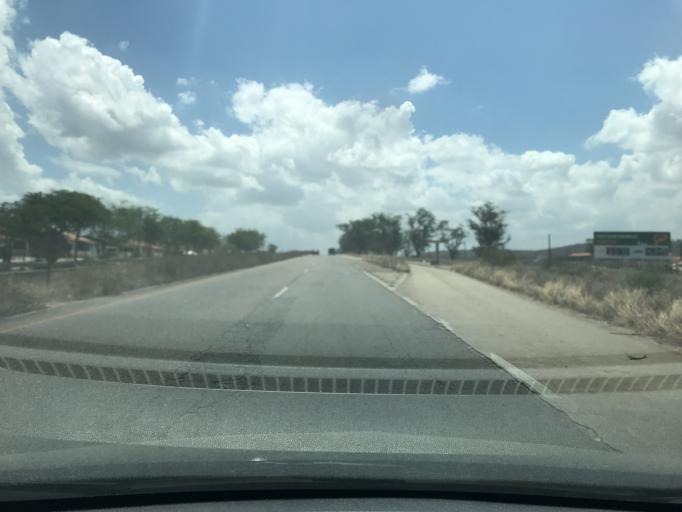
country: BR
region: Pernambuco
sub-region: Bezerros
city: Bezerros
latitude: -8.2971
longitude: -35.8664
